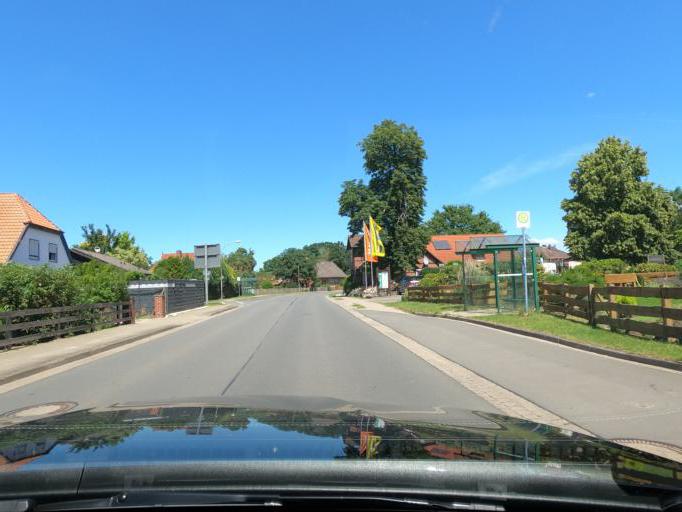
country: DE
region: Lower Saxony
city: Eicklingen
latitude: 52.5589
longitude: 10.1829
